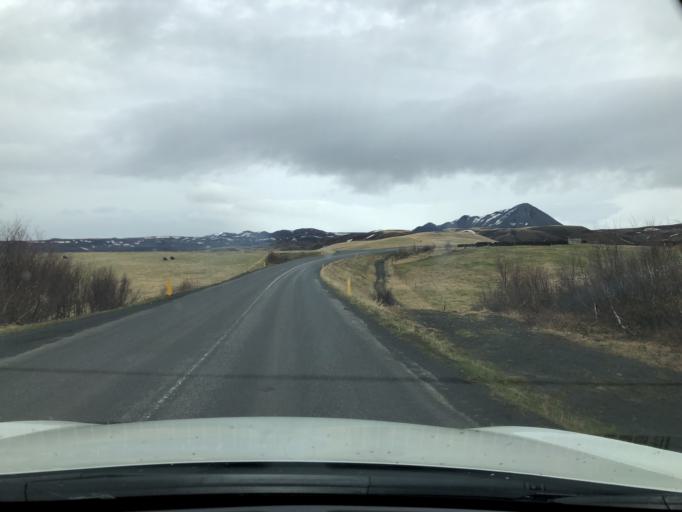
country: IS
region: Northeast
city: Laugar
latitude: 65.6336
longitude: -16.9192
